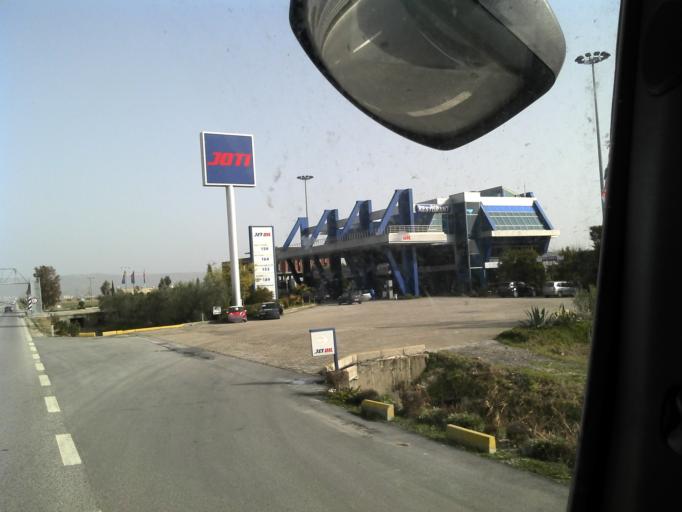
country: AL
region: Fier
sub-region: Rrethi i Lushnjes
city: Krutja e Poshtme
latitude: 40.8858
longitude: 19.6756
